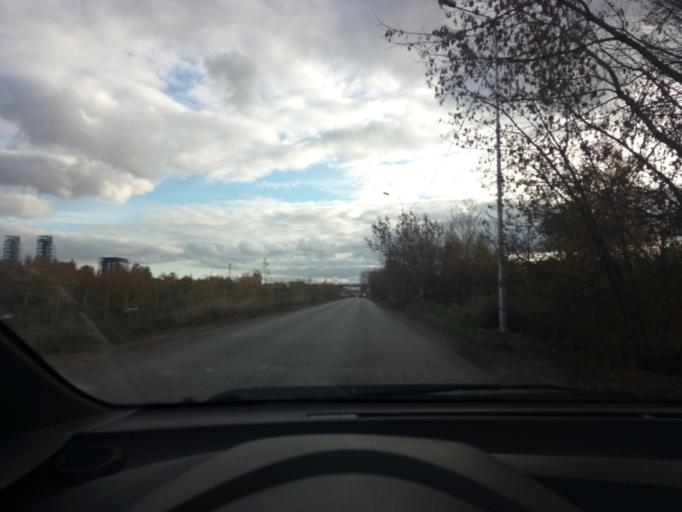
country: RU
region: Tatarstan
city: Staroye Arakchino
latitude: 55.8845
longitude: 48.9761
